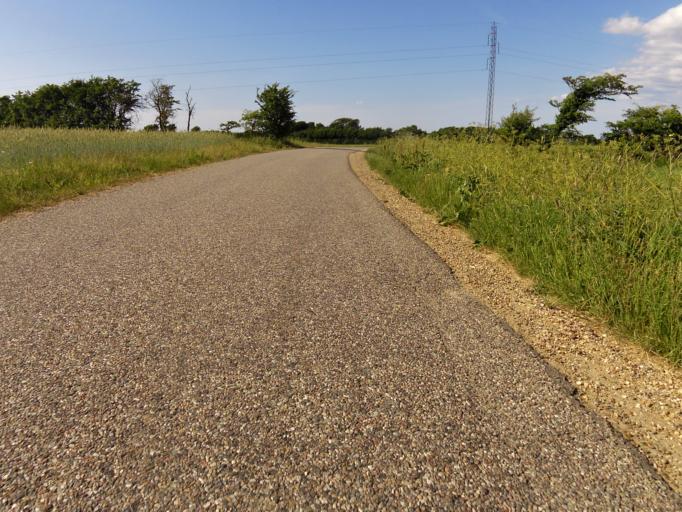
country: DK
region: Central Jutland
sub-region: Holstebro Kommune
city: Vinderup
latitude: 56.4594
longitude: 8.8485
